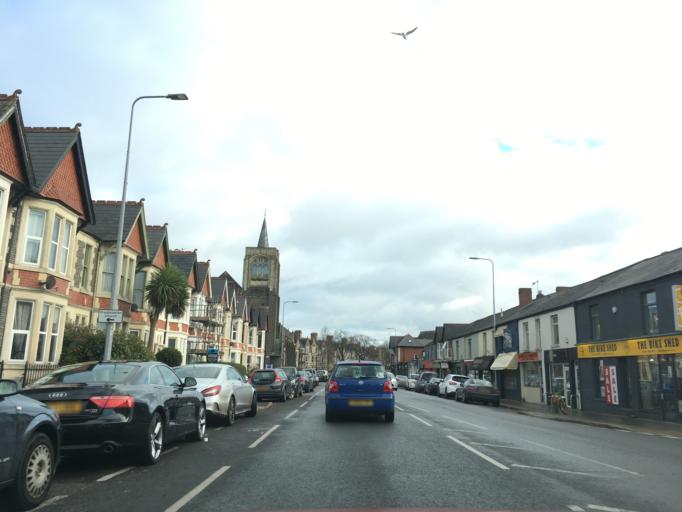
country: GB
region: Wales
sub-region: Cardiff
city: Cardiff
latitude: 51.4892
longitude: -3.2022
